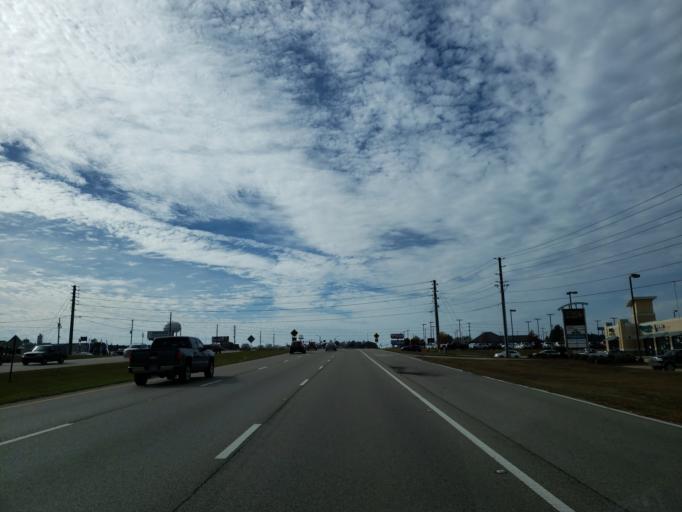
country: US
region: Mississippi
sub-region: Lamar County
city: West Hattiesburg
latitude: 31.3184
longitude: -89.4038
